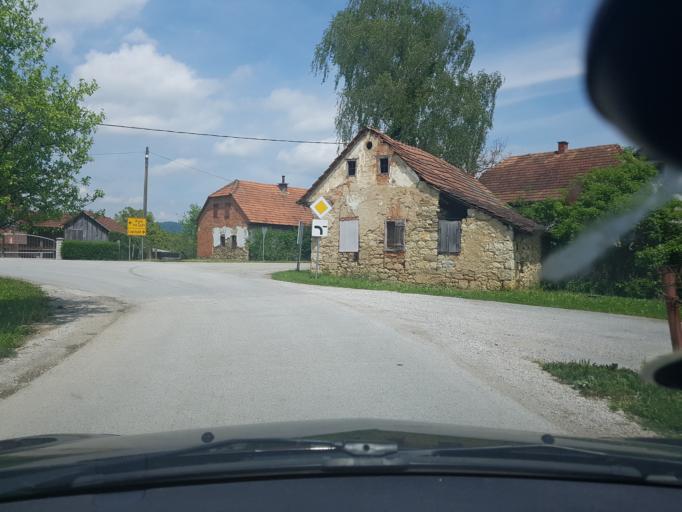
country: SI
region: Rogatec
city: Rogatec
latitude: 46.2076
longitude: 15.7290
